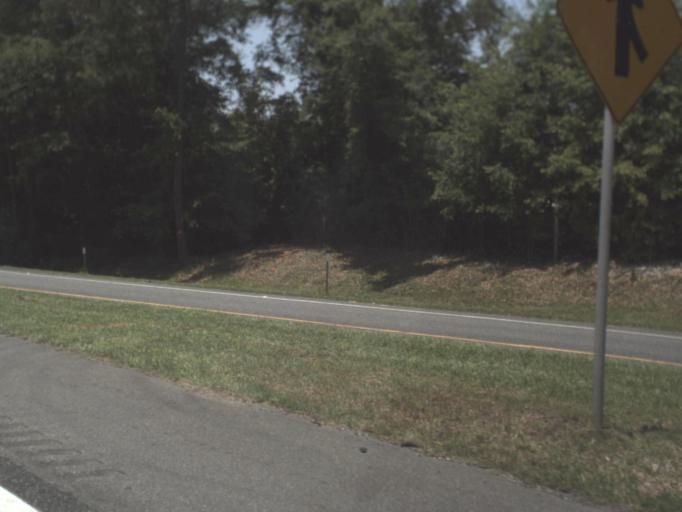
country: US
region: Florida
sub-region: Baker County
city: Macclenny
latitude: 30.2617
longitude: -82.1076
